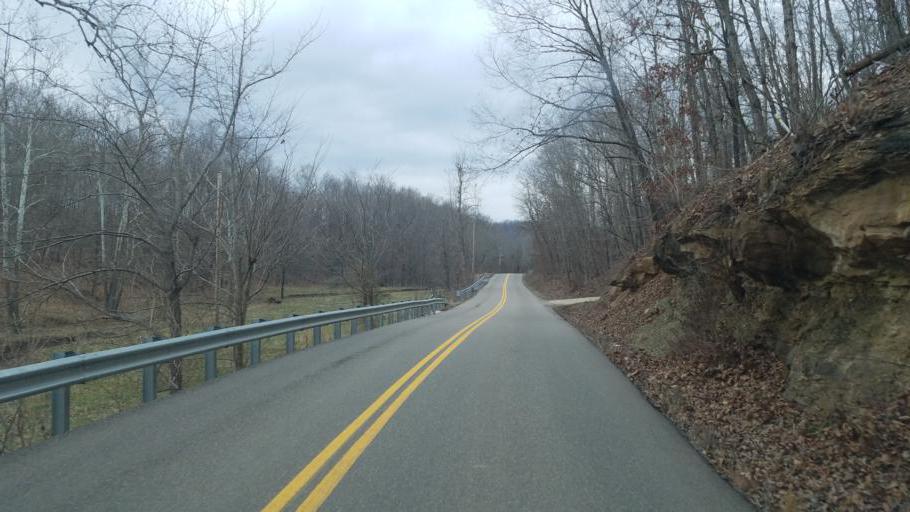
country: US
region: Ohio
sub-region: Gallia County
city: Gallipolis
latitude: 38.7182
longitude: -82.3478
